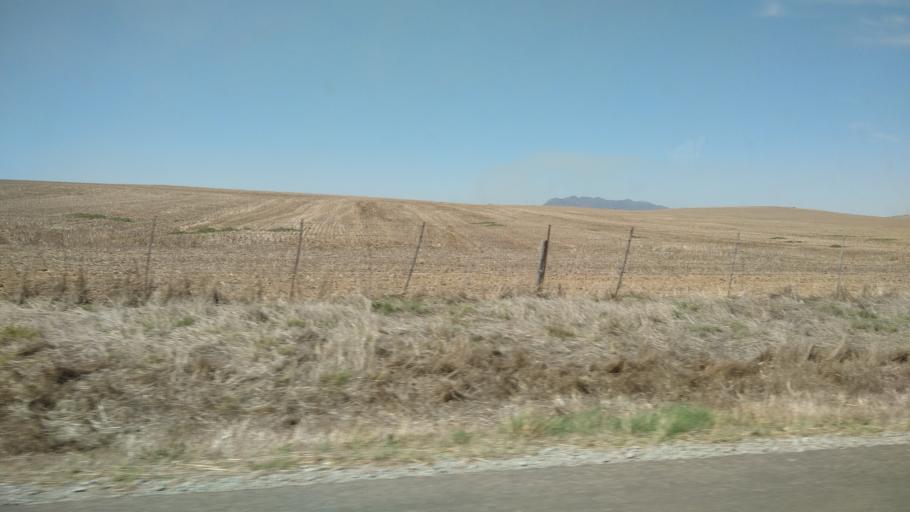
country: ZA
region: Western Cape
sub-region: West Coast District Municipality
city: Malmesbury
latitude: -33.3469
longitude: 18.6395
